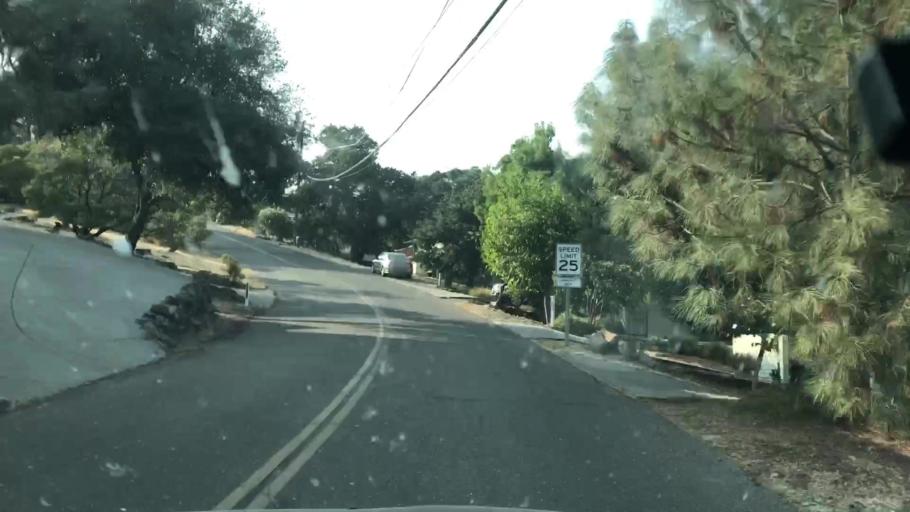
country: US
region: California
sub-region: Lake County
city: Hidden Valley Lake
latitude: 38.8151
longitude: -122.5688
